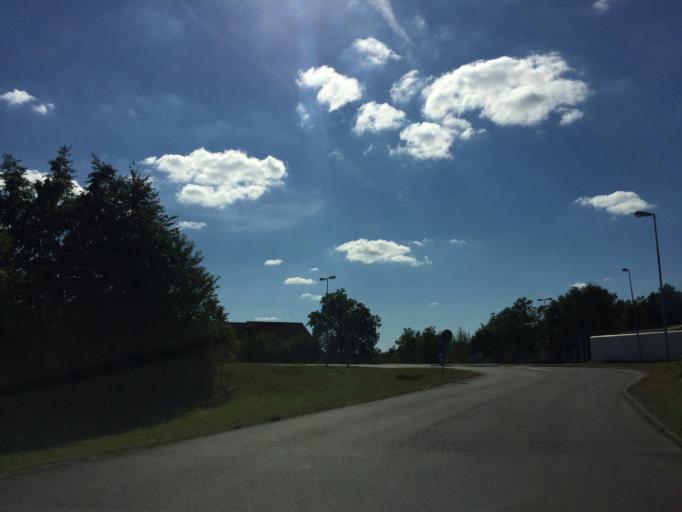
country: SE
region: Stockholm
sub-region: Sollentuna Kommun
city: Sollentuna
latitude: 59.4589
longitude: 17.9106
